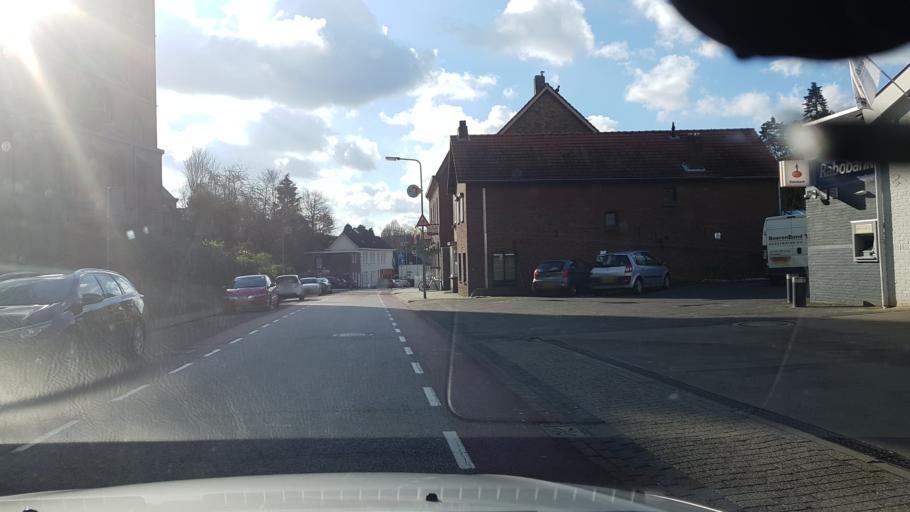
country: NL
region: Limburg
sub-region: Valkenburg aan de Geul
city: Houthem
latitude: 50.9066
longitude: 5.7845
